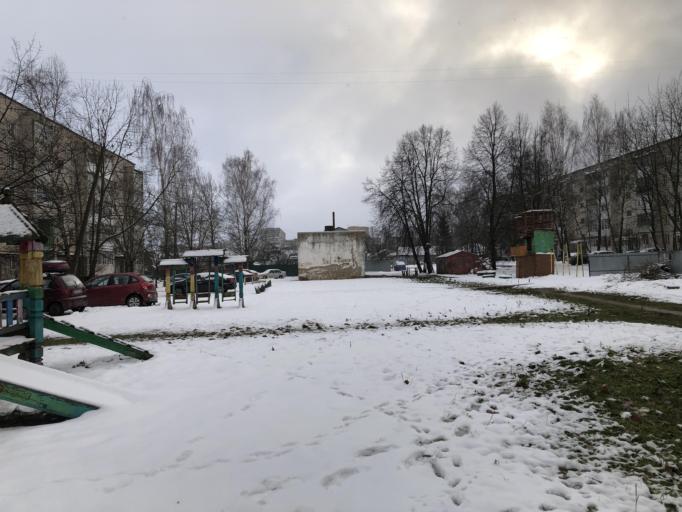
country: RU
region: Smolensk
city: Safonovo
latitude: 55.1151
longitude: 33.2422
